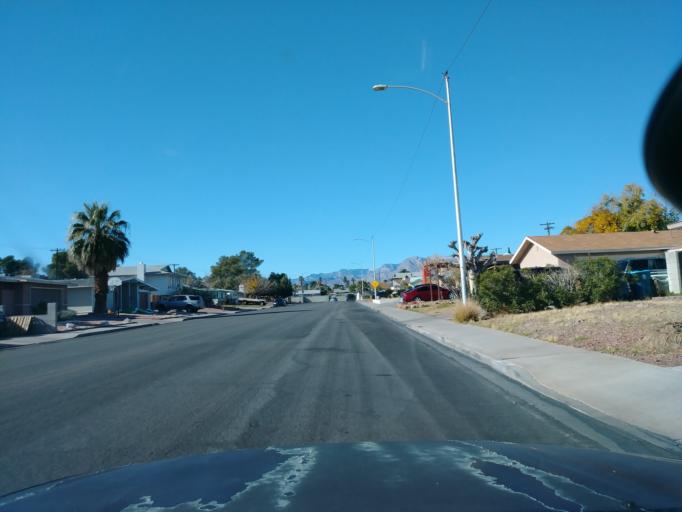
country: US
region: Nevada
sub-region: Clark County
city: Spring Valley
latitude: 36.1759
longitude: -115.2309
